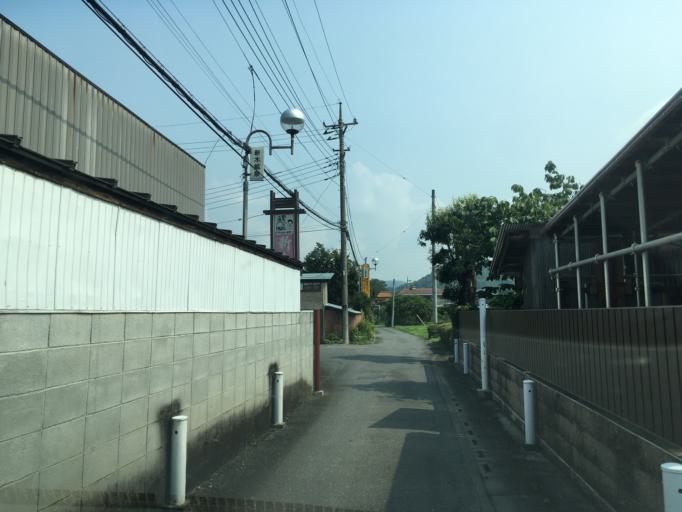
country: JP
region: Saitama
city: Chichibu
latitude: 36.0093
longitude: 139.1104
